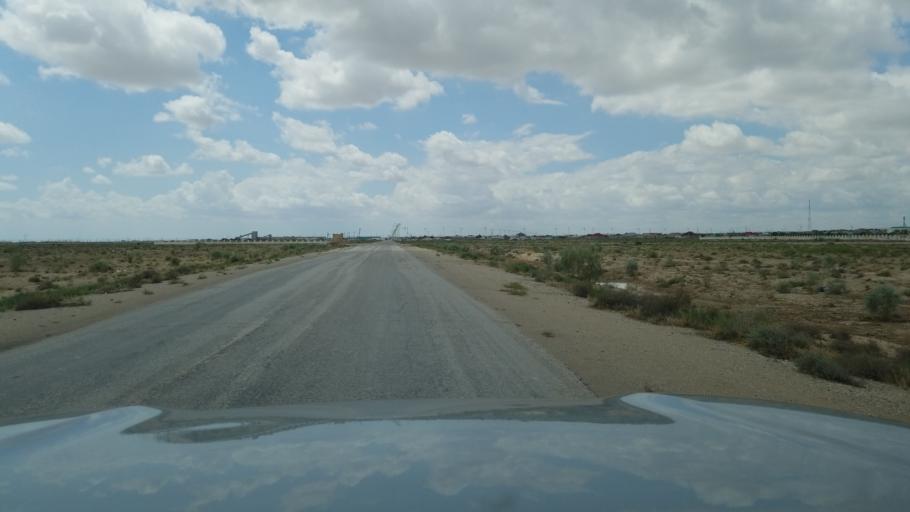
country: TM
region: Balkan
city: Balkanabat
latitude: 39.4892
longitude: 54.4026
